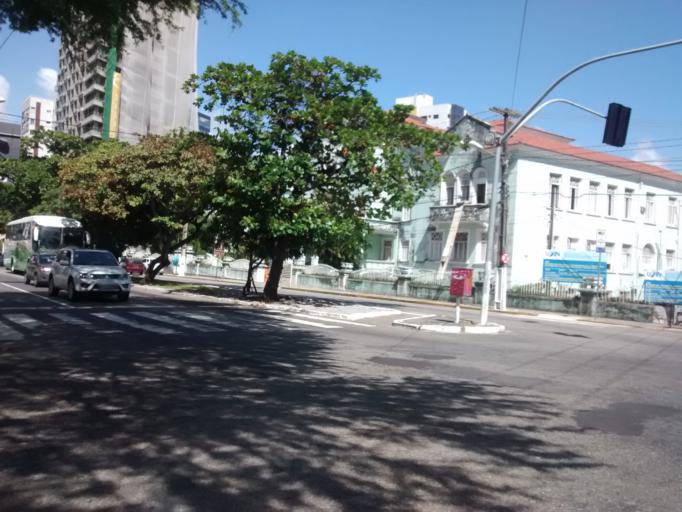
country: BR
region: Rio Grande do Norte
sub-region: Natal
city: Natal
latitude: -5.7817
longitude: -35.1973
